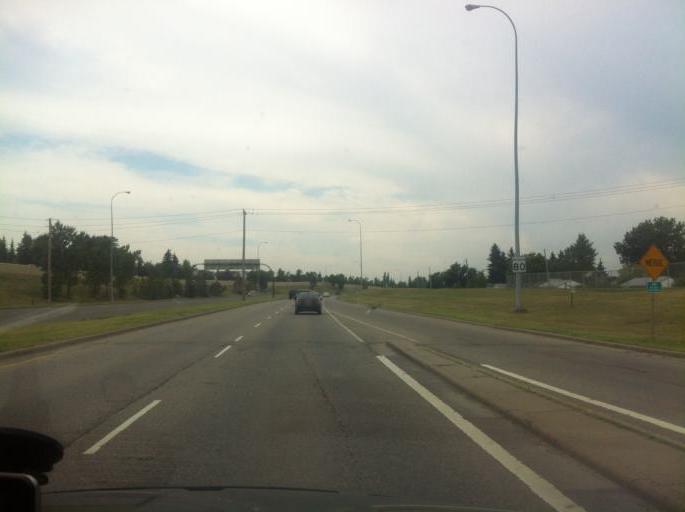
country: CA
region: Alberta
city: Calgary
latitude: 50.9470
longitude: -114.0263
